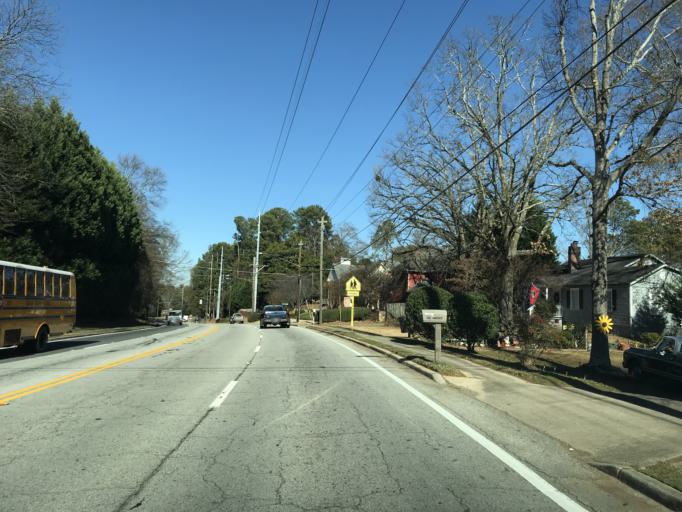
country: US
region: Georgia
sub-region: DeKalb County
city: Tucker
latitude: 33.8643
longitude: -84.2181
